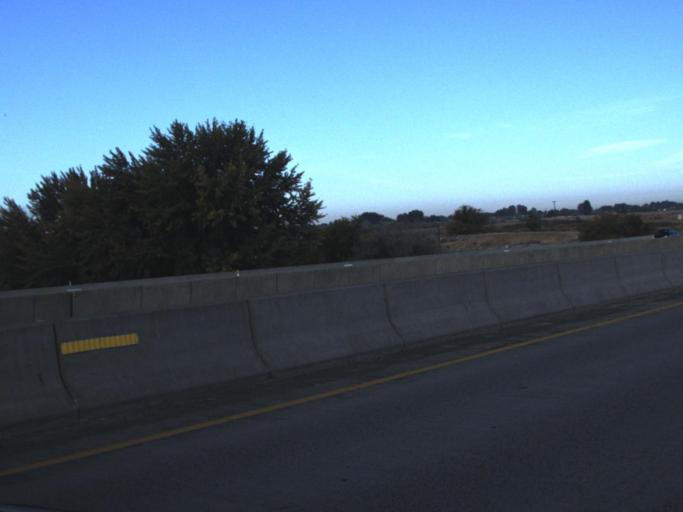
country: US
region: Washington
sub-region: Benton County
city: Prosser
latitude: 46.2171
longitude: -119.7469
